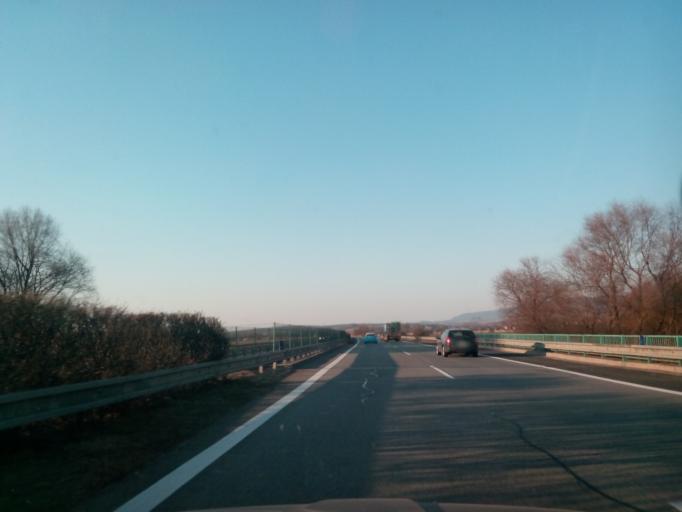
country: SK
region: Kosicky
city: Kosice
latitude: 48.8178
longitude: 21.3104
